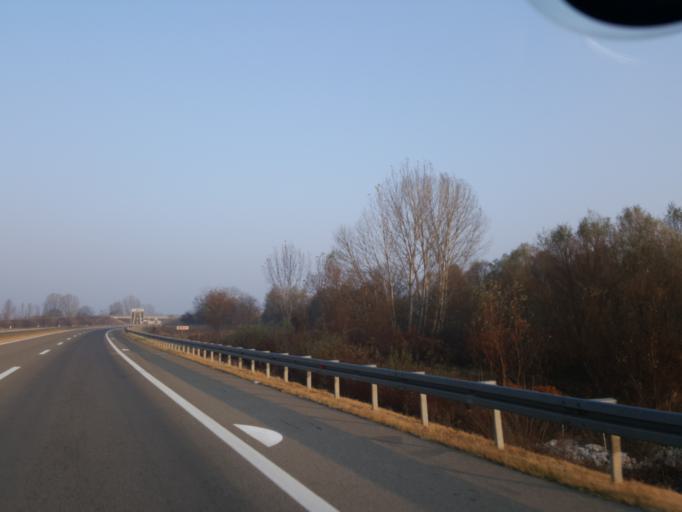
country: RS
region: Central Serbia
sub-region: Jablanicki Okrug
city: Vlasotince
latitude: 42.9200
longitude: 22.0319
